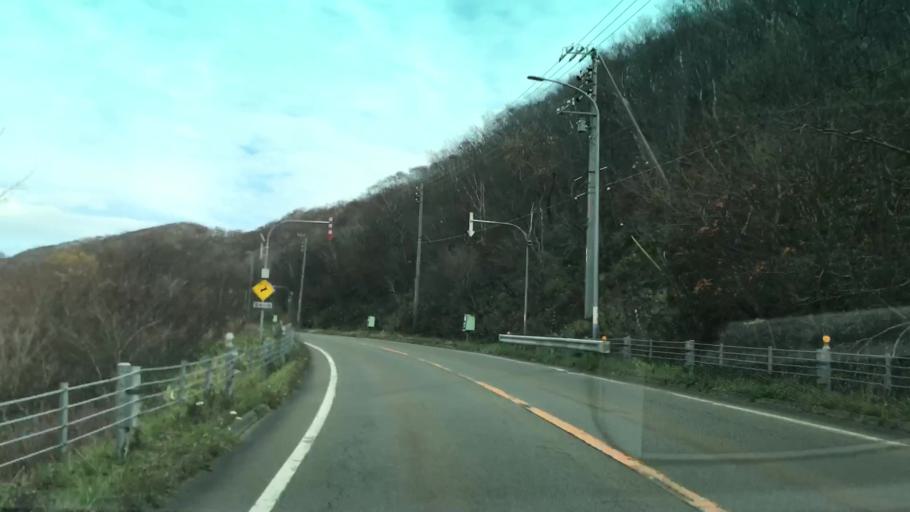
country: JP
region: Hokkaido
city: Obihiro
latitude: 42.0254
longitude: 143.2154
